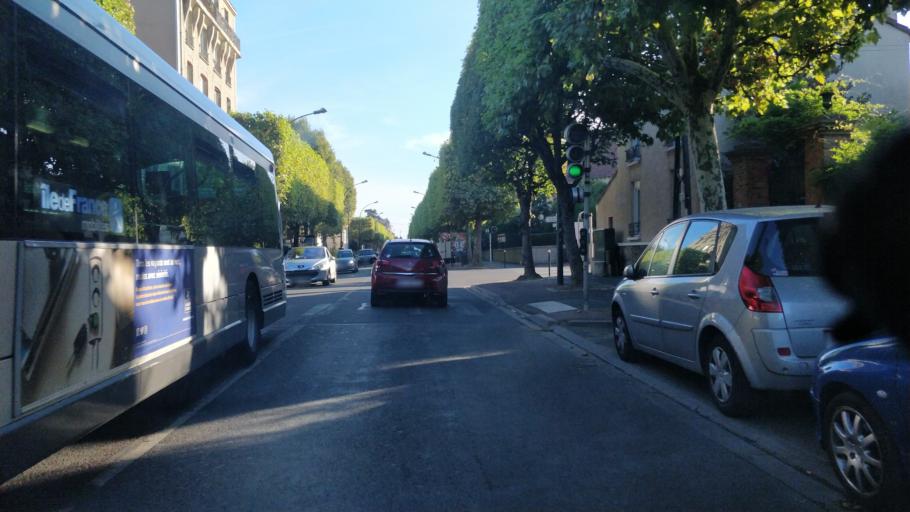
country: FR
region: Ile-de-France
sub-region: Departement de Seine-Saint-Denis
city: Le Raincy
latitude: 48.9030
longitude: 2.5207
